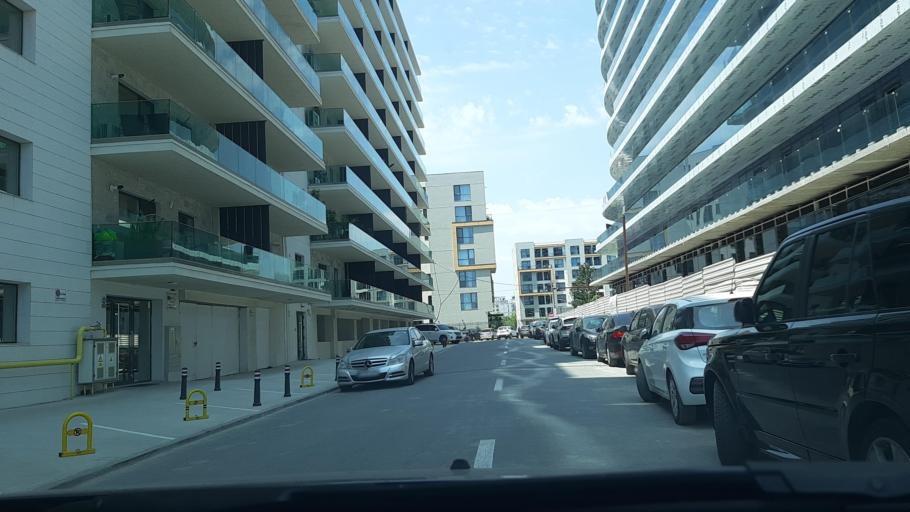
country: RO
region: Constanta
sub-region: Comuna Navodari
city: Navodari
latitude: 44.2890
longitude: 28.6228
